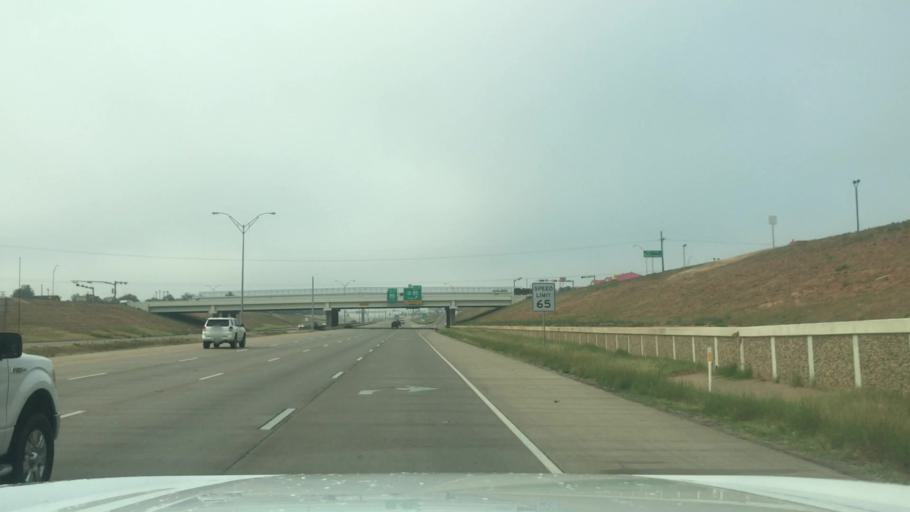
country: US
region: Texas
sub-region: Lubbock County
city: Lubbock
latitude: 33.5509
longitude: -101.8453
